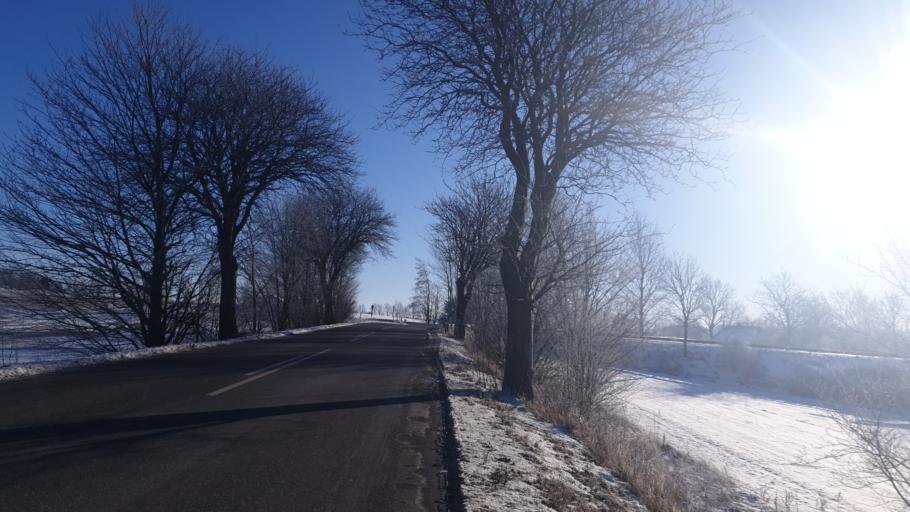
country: DK
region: Central Jutland
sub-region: Hedensted Kommune
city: Hedensted
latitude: 55.7968
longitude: 9.7442
